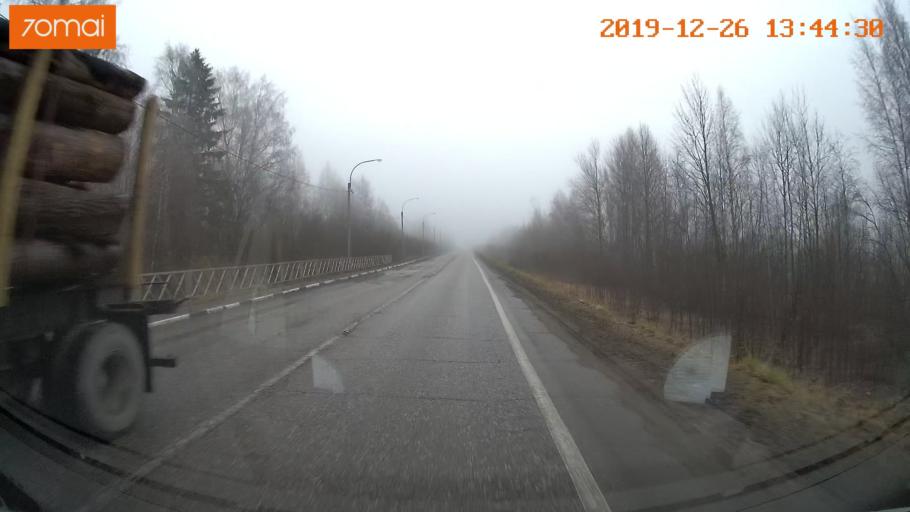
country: RU
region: Vologda
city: Sheksna
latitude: 58.7015
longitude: 38.5073
